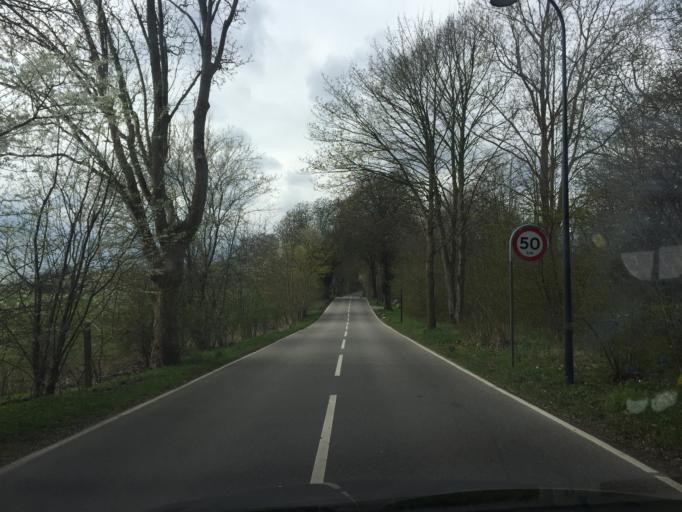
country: DK
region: Capital Region
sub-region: Rudersdal Kommune
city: Trorod
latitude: 55.8485
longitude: 12.5174
